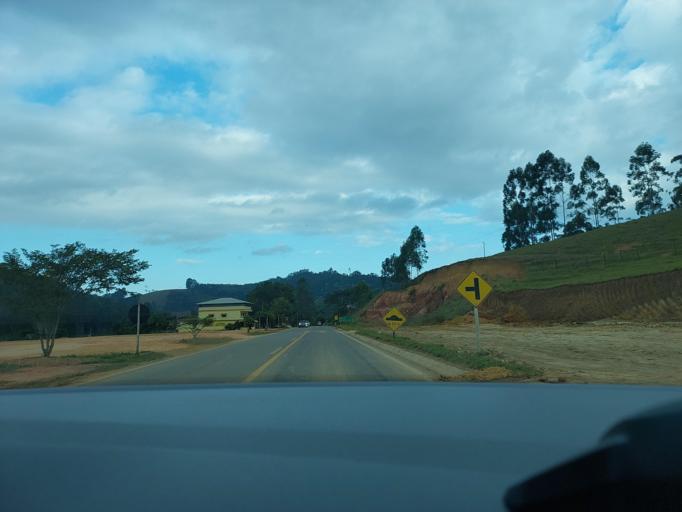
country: BR
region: Minas Gerais
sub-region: Mirai
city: Mirai
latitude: -20.9961
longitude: -42.5572
